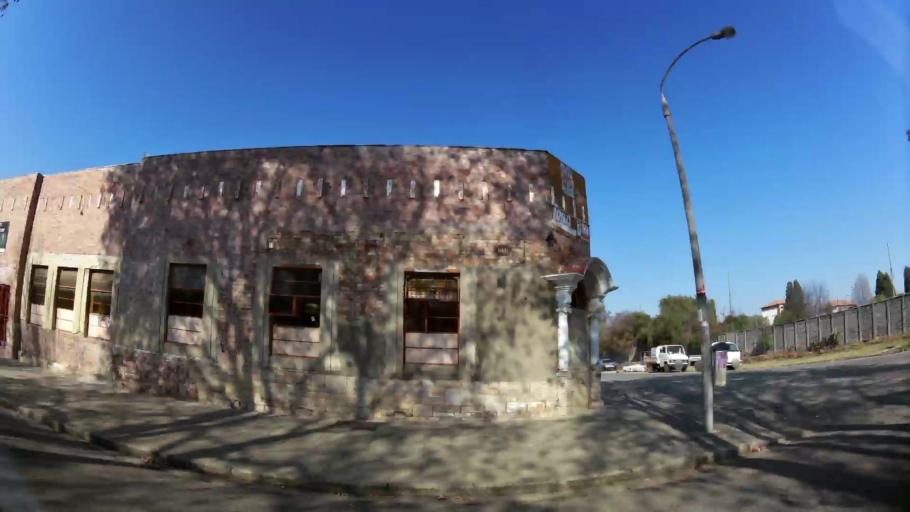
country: ZA
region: Gauteng
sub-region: Ekurhuleni Metropolitan Municipality
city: Boksburg
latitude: -26.2205
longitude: 28.2421
